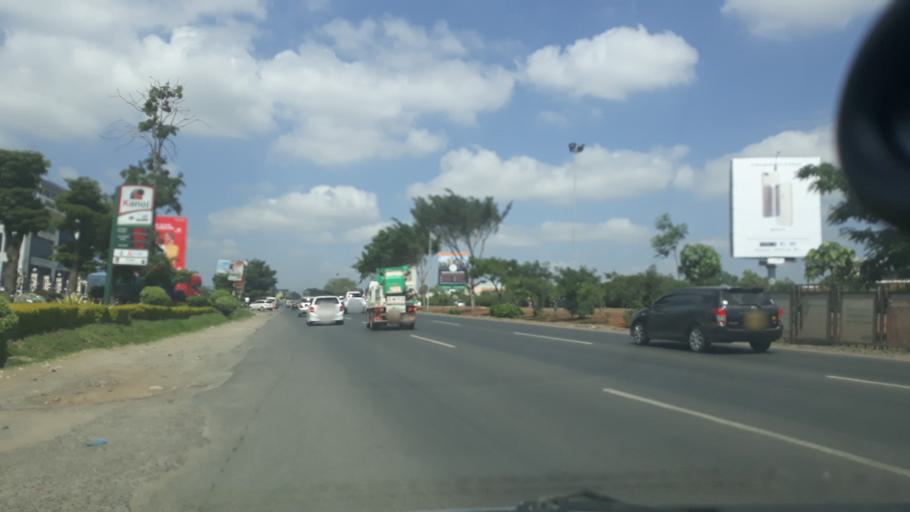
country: KE
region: Nairobi Area
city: Pumwani
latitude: -1.3190
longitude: 36.8371
